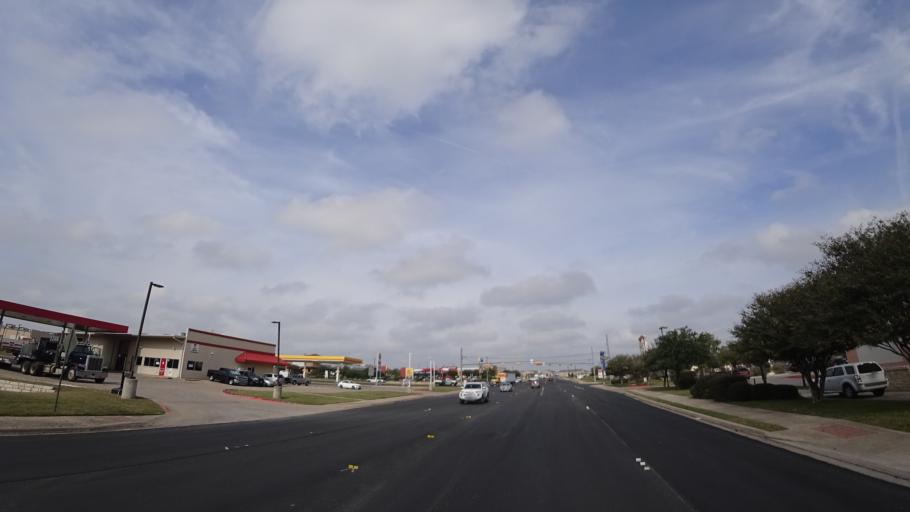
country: US
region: Texas
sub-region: Travis County
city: Windemere
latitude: 30.4550
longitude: -97.6596
